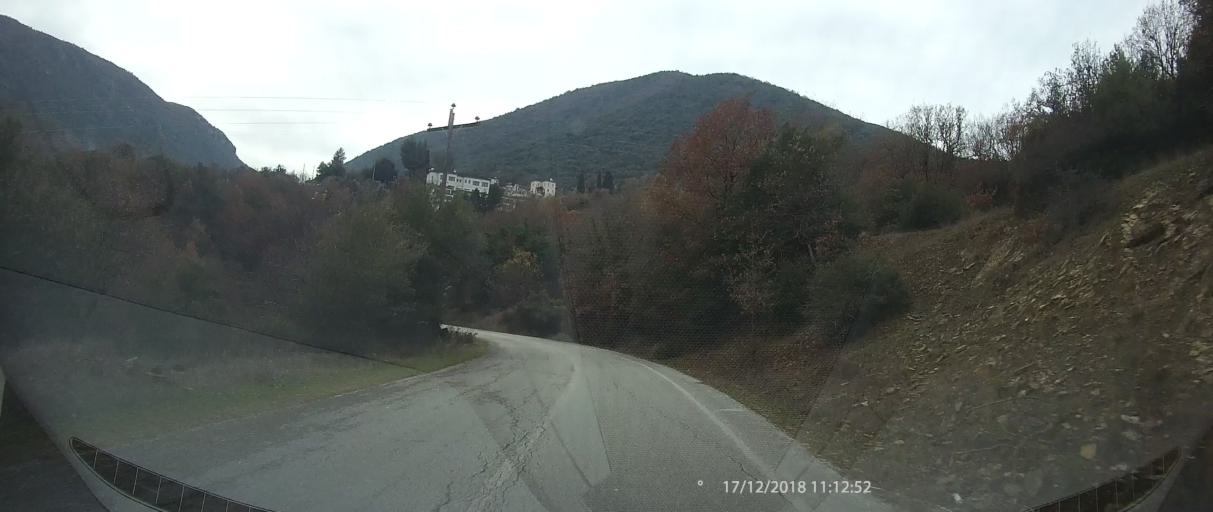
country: GR
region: Epirus
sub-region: Nomos Ioanninon
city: Kalpaki
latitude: 39.9384
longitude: 20.6716
